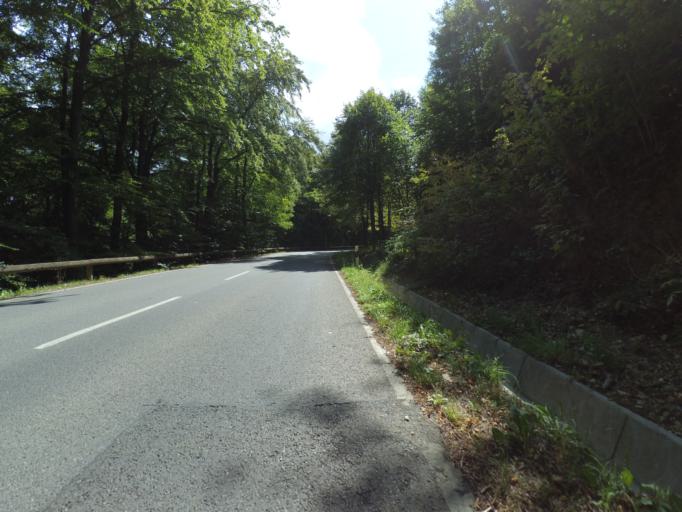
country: LU
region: Luxembourg
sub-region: Canton de Luxembourg
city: Niederanven
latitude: 49.6595
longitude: 6.2293
